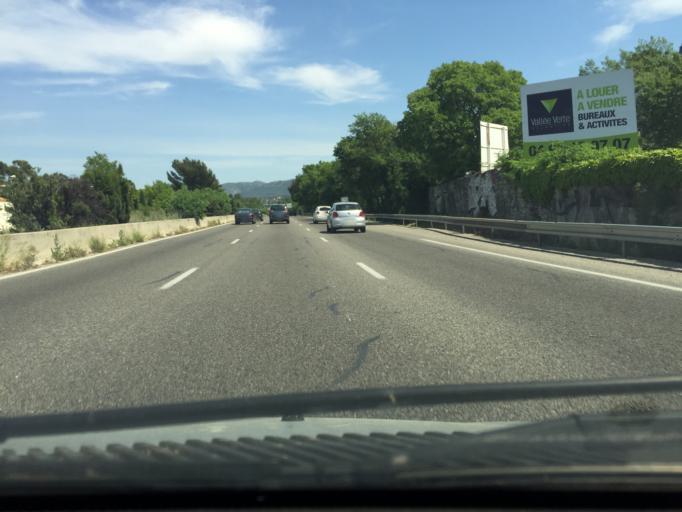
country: FR
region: Provence-Alpes-Cote d'Azur
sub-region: Departement des Bouches-du-Rhone
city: La Penne-sur-Huveaune
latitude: 43.2889
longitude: 5.4966
